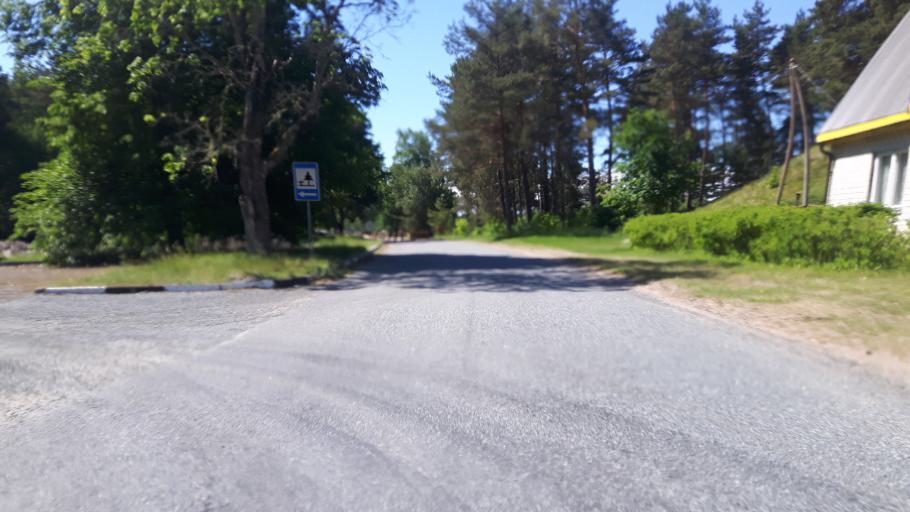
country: EE
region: Paernumaa
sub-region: Paernu linn
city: Parnu
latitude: 58.1286
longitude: 24.5094
